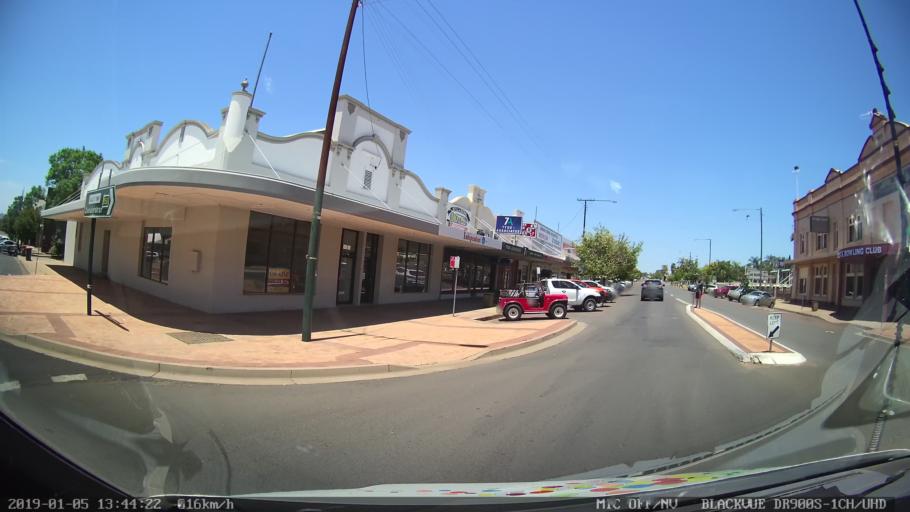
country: AU
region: New South Wales
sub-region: Gunnedah
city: Gunnedah
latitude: -30.9794
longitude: 150.2564
